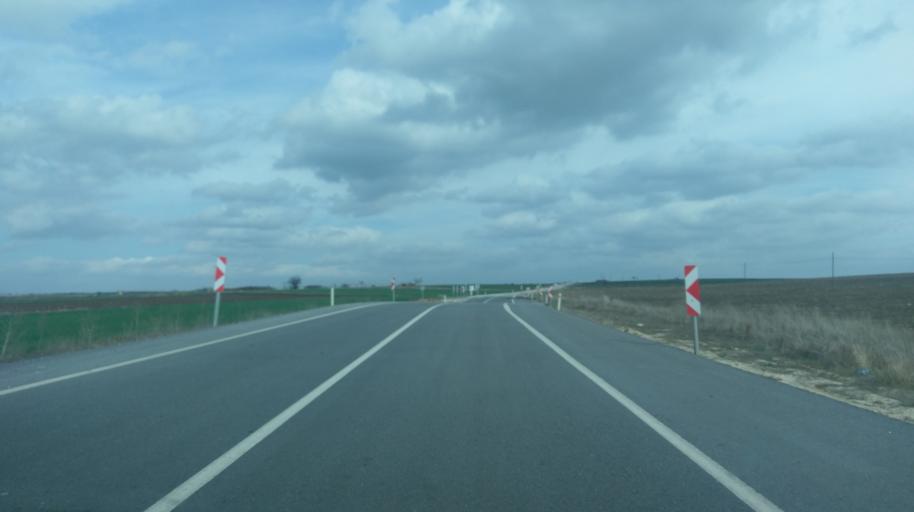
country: TR
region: Edirne
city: Haskoy
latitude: 41.6613
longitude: 26.9313
